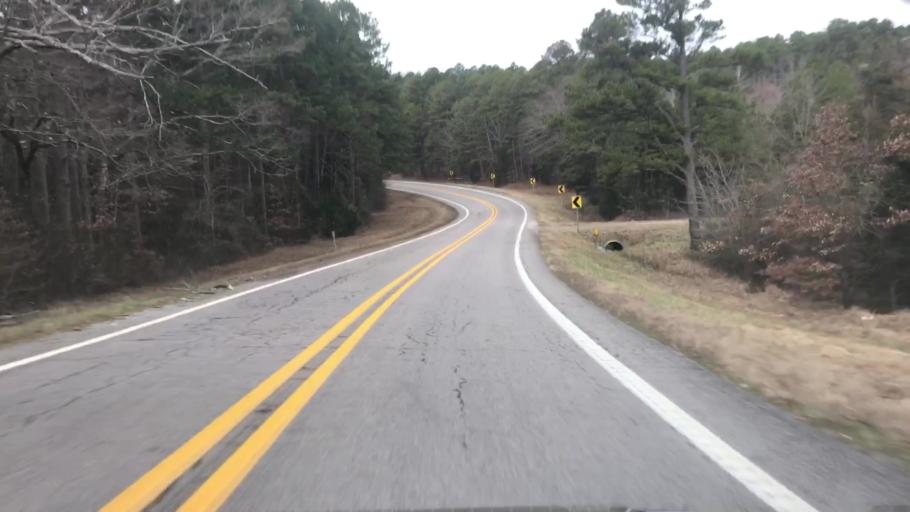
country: US
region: Arkansas
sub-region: Montgomery County
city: Mount Ida
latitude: 34.6697
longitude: -93.7768
